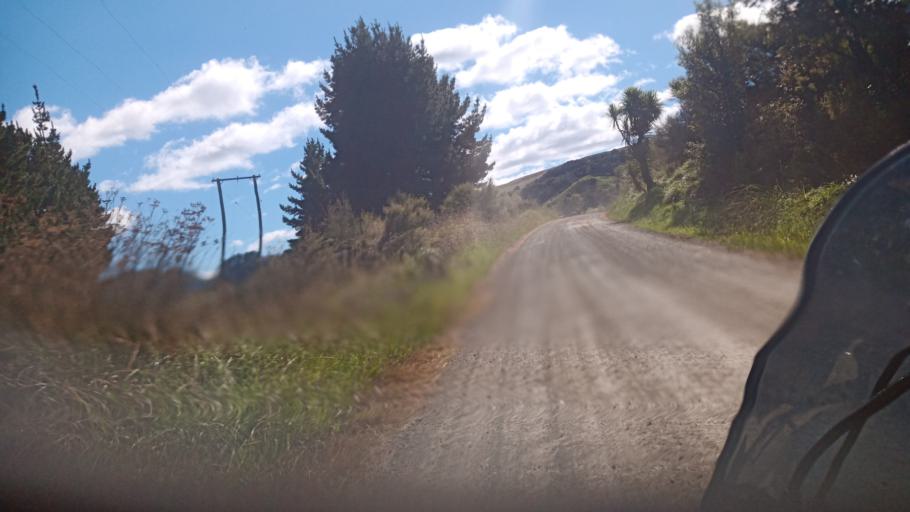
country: NZ
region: Gisborne
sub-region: Gisborne District
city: Gisborne
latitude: -38.4052
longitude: 177.6774
